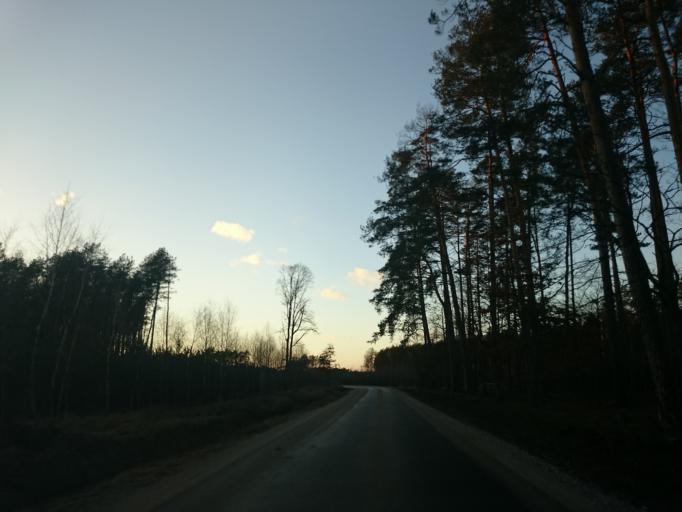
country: PL
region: Kujawsko-Pomorskie
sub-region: Powiat golubsko-dobrzynski
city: Ciechocin
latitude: 53.0989
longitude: 18.9294
